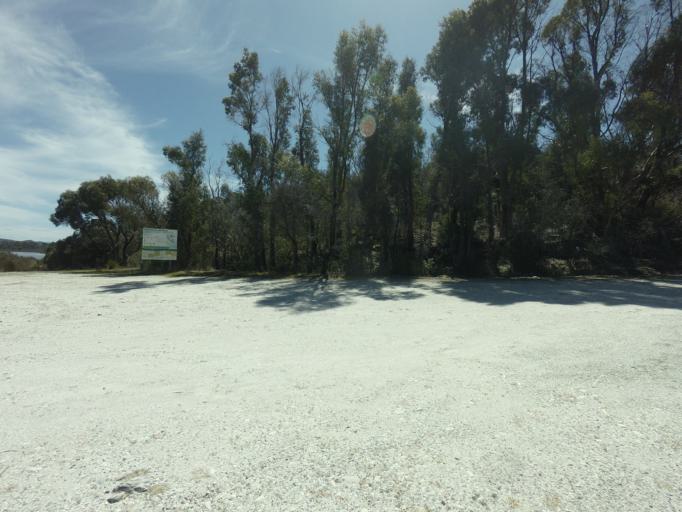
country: AU
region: Tasmania
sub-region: Huon Valley
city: Geeveston
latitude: -42.8505
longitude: 146.1753
